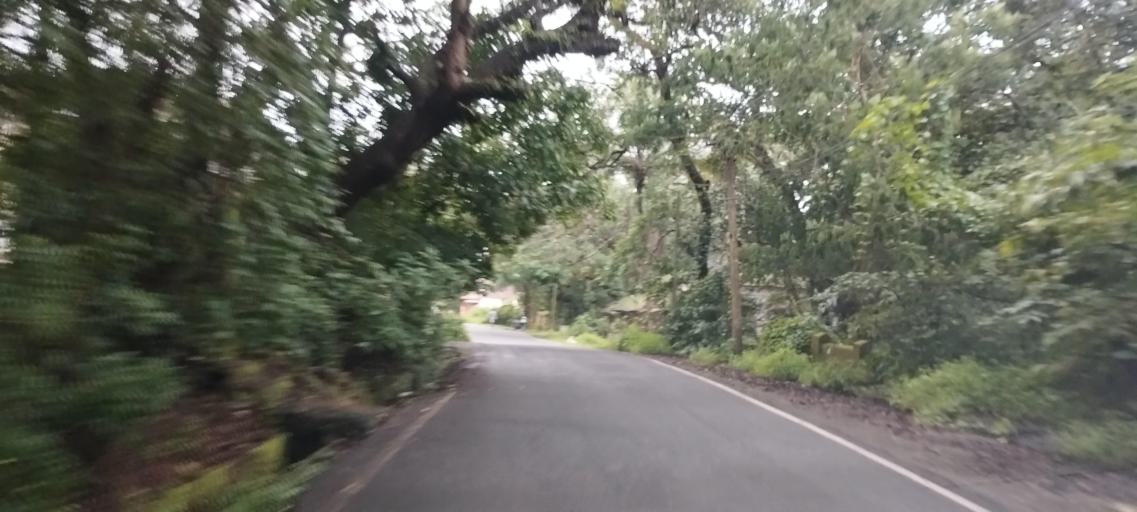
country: IN
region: Goa
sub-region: North Goa
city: Jua
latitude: 15.5234
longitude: 73.9009
